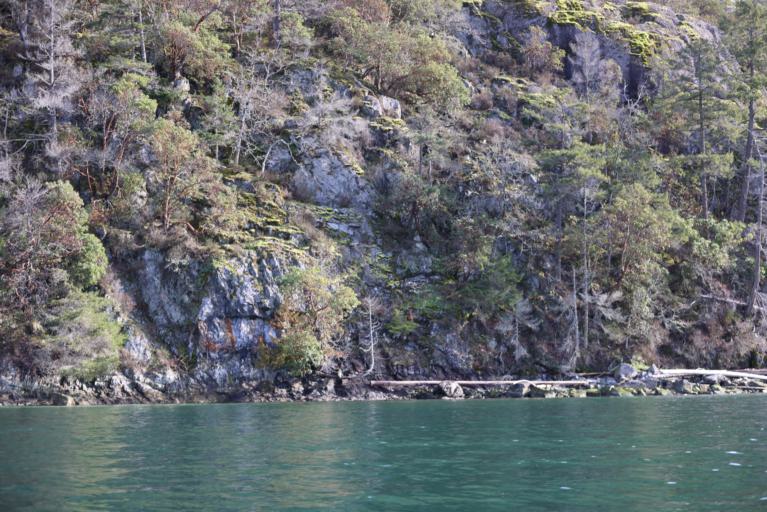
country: CA
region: British Columbia
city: Duncan
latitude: 48.7566
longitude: -123.5910
